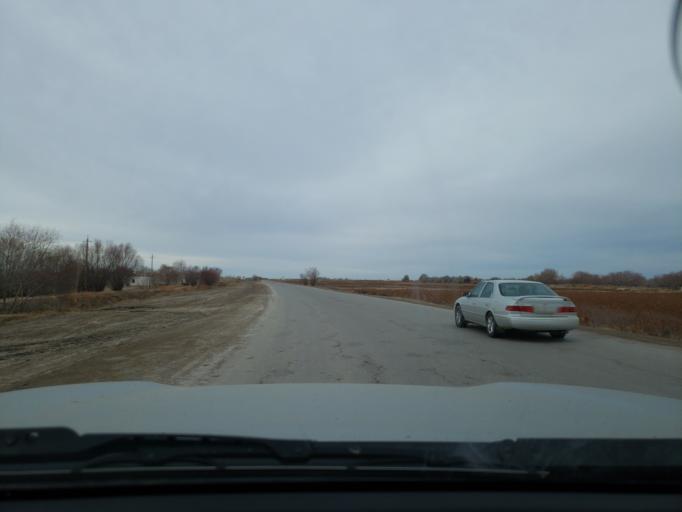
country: TM
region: Dasoguz
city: Boldumsaz
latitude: 42.1569
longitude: 59.6115
